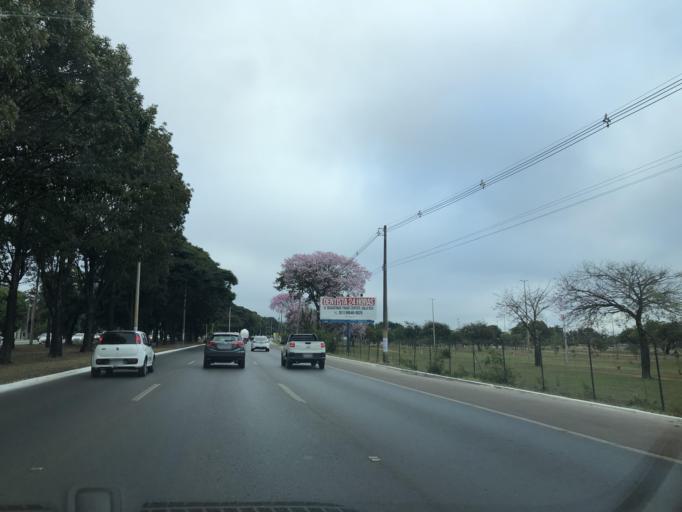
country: BR
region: Federal District
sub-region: Brasilia
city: Brasilia
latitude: -15.8224
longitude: -48.0557
